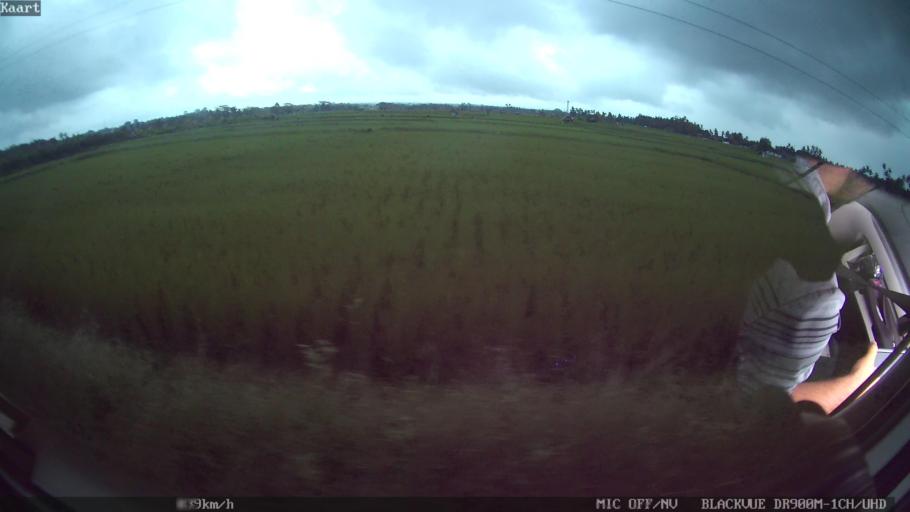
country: ID
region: Bali
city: Banjar Keraman
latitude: -8.5233
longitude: 115.2245
